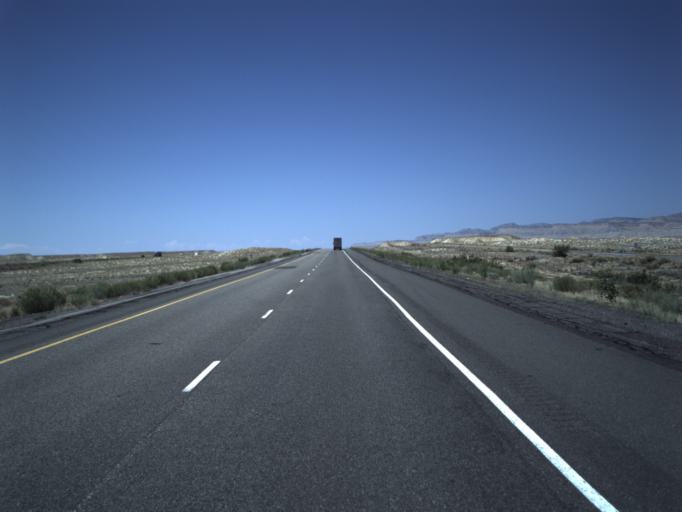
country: US
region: Utah
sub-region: Grand County
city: Moab
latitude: 38.9383
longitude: -109.4856
